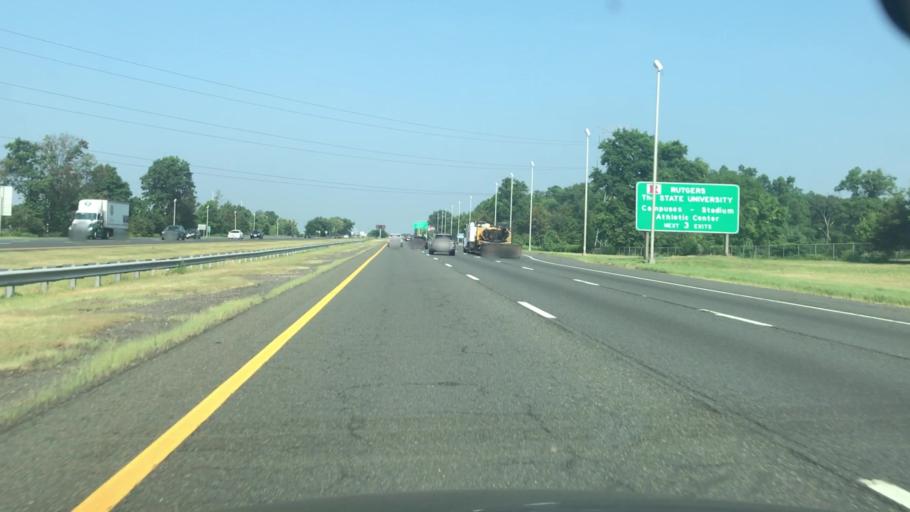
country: US
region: New Jersey
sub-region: Middlesex County
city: Society Hill
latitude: 40.5557
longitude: -74.4533
